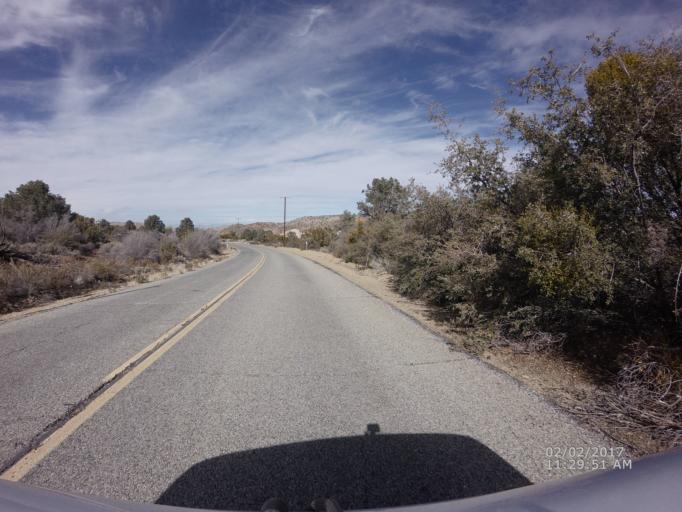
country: US
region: California
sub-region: Los Angeles County
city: Littlerock
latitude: 34.4283
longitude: -117.8707
